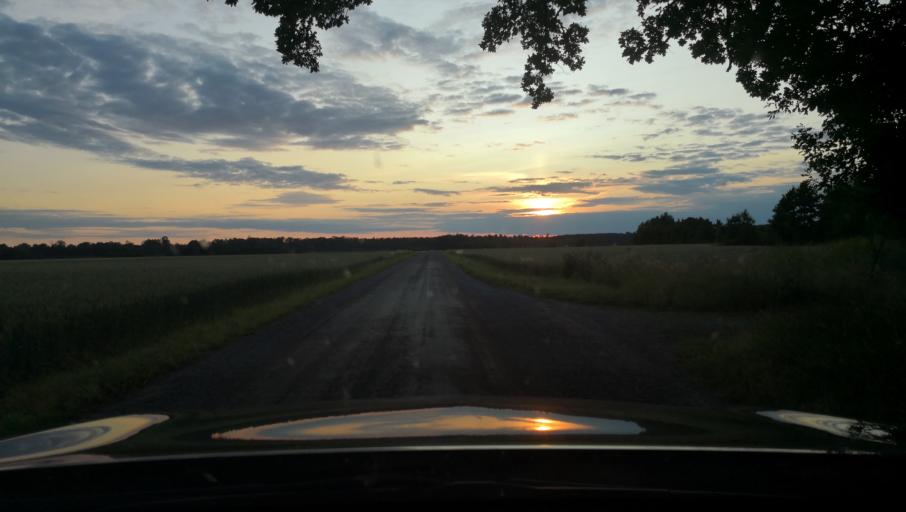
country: SE
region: Uppsala
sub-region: Osthammars Kommun
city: Bjorklinge
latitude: 60.0555
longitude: 17.5959
